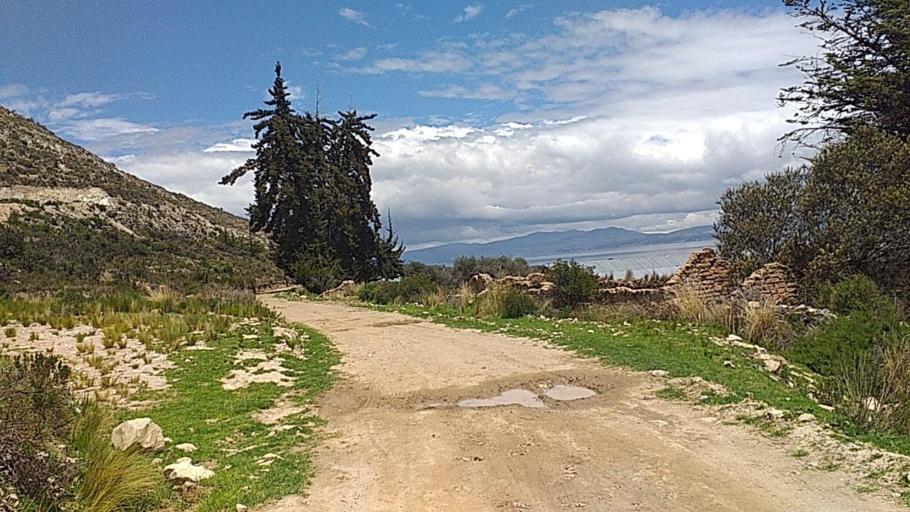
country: BO
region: La Paz
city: Huatajata
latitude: -16.3189
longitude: -68.6701
